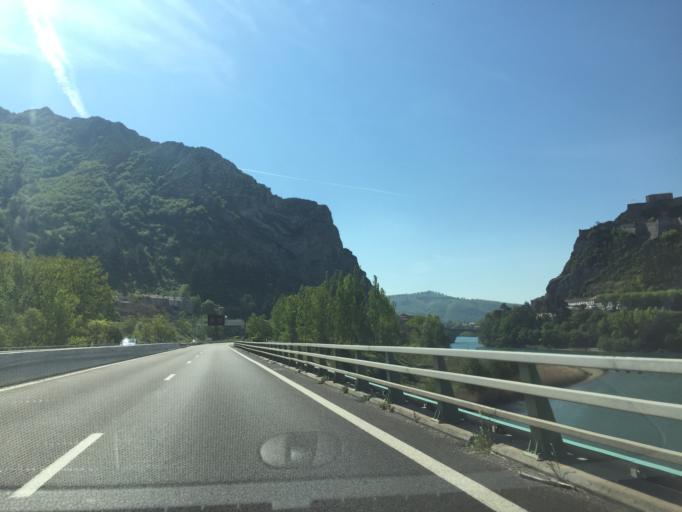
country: FR
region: Provence-Alpes-Cote d'Azur
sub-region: Departement des Alpes-de-Haute-Provence
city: Sisteron
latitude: 44.2044
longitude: 5.9422
